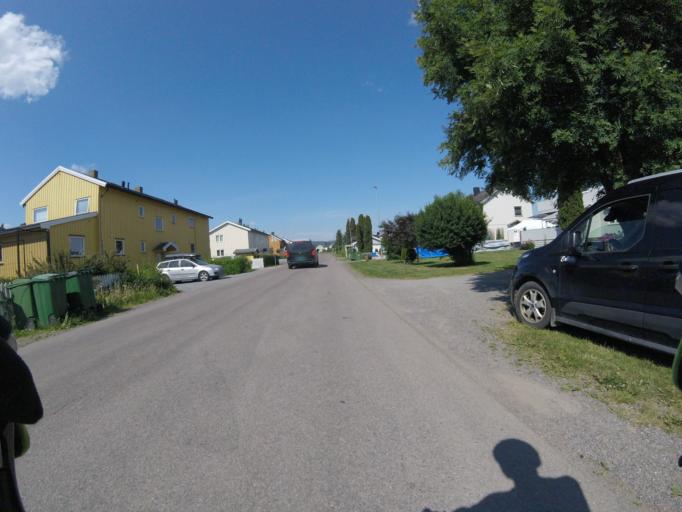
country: NO
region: Akershus
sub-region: Skedsmo
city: Lillestrom
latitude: 59.9610
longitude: 11.0454
